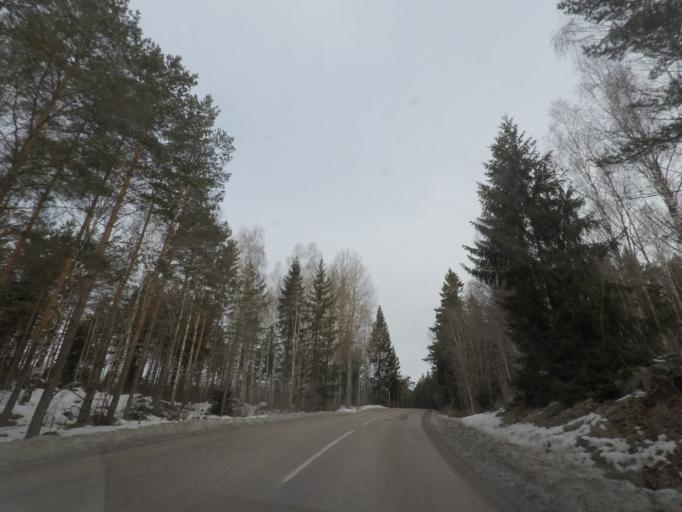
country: SE
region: Vaestmanland
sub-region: Vasteras
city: Skultuna
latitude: 59.7485
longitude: 16.3268
